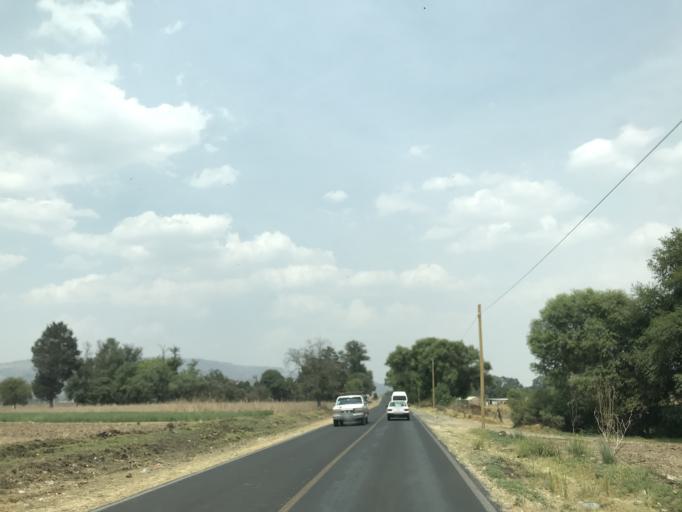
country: MX
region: Tlaxcala
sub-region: Ixtacuixtla de Mariano Matamoros
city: Santa Justina Ecatepec
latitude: 19.3157
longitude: -98.3246
